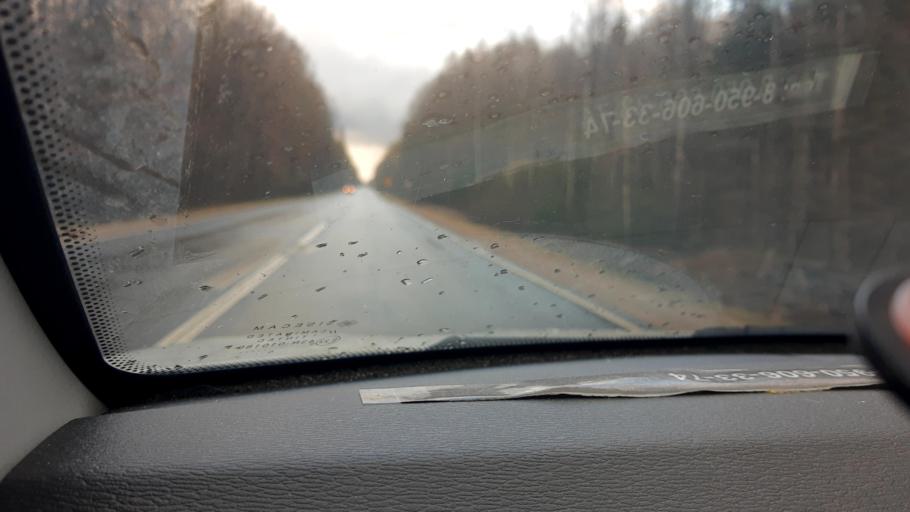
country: RU
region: Nizjnij Novgorod
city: Uren'
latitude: 57.2517
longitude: 45.6047
